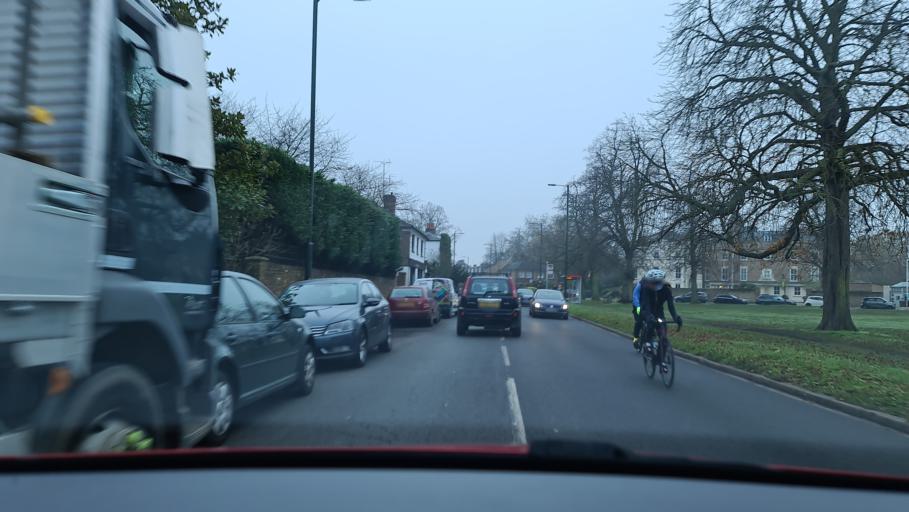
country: GB
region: England
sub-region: Greater London
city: Kingston upon Thames
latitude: 51.4335
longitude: -0.3063
